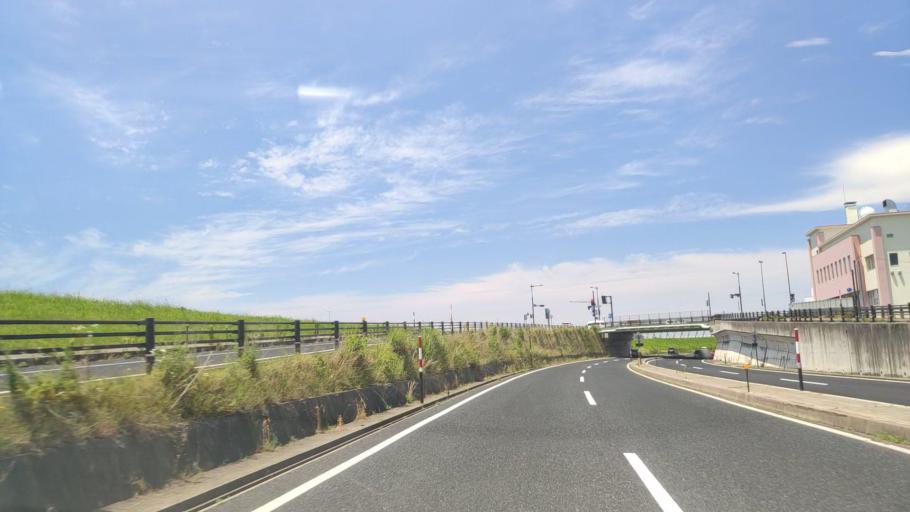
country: JP
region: Tottori
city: Tottori
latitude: 35.4950
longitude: 134.2179
